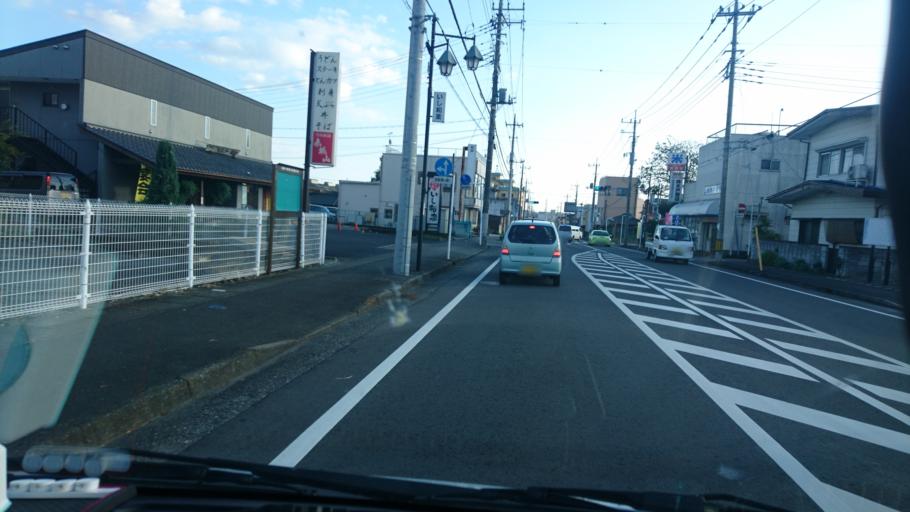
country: JP
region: Gunma
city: Omamacho-omama
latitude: 36.4337
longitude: 139.2771
